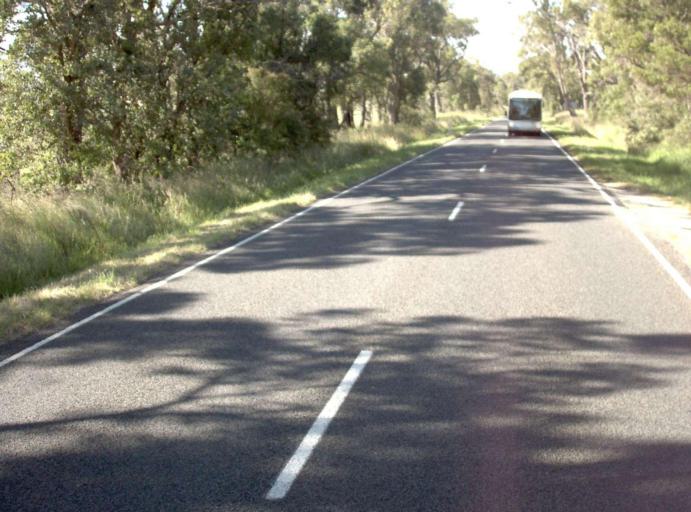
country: AU
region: Victoria
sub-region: Latrobe
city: Traralgon
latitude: -38.1517
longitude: 146.4937
